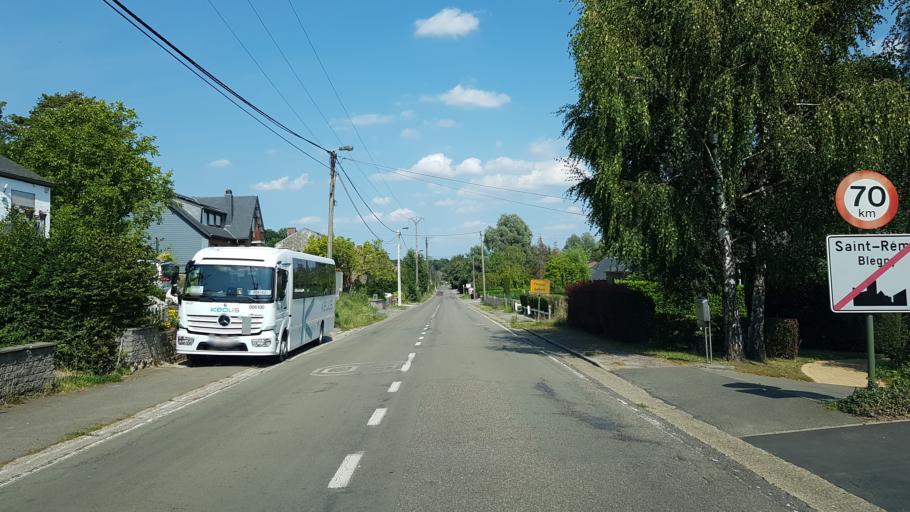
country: BE
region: Wallonia
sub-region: Province de Liege
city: Dalhem
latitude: 50.7004
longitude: 5.7028
